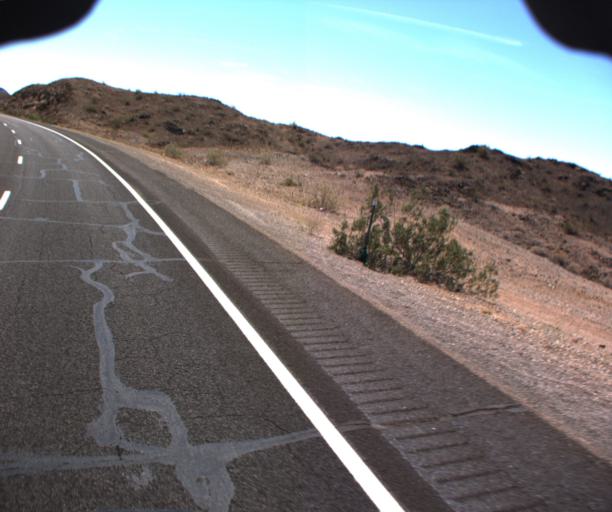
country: US
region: Arizona
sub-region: La Paz County
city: Cienega Springs
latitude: 34.1986
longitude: -114.2099
